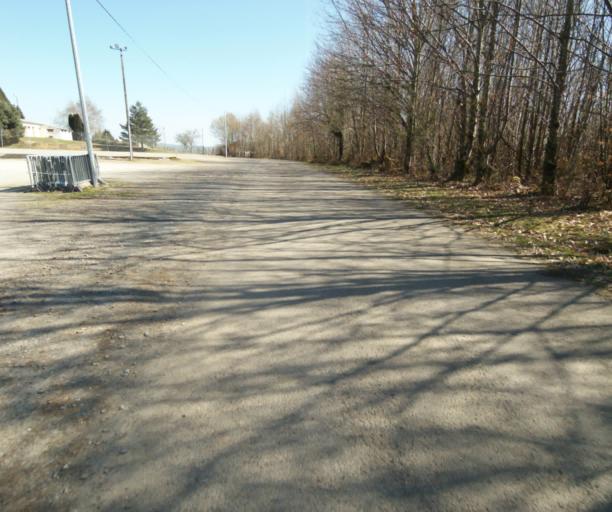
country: FR
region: Limousin
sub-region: Departement de la Correze
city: Chameyrat
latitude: 45.2513
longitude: 1.7111
